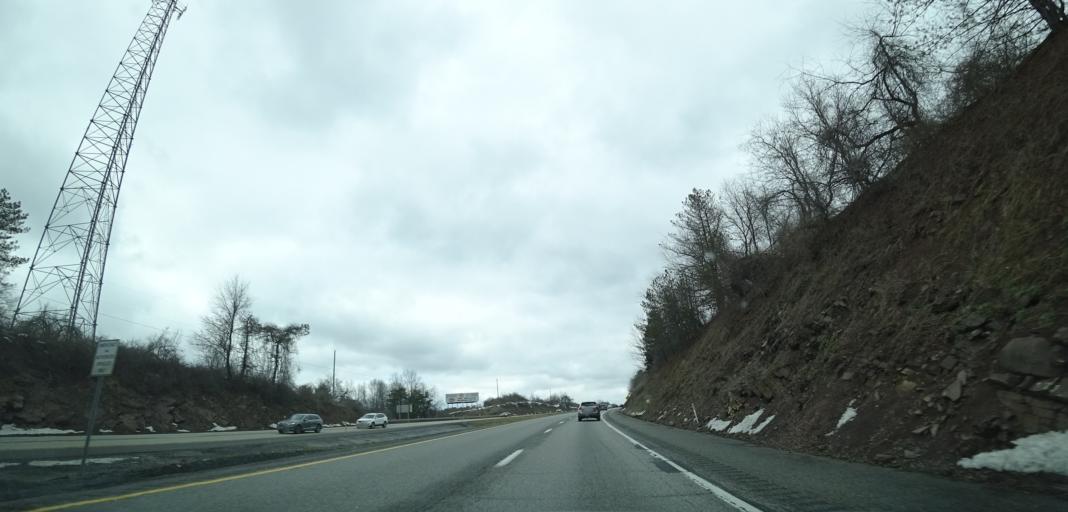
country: US
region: Pennsylvania
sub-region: Bedford County
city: Earlston
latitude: 39.9636
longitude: -78.2472
